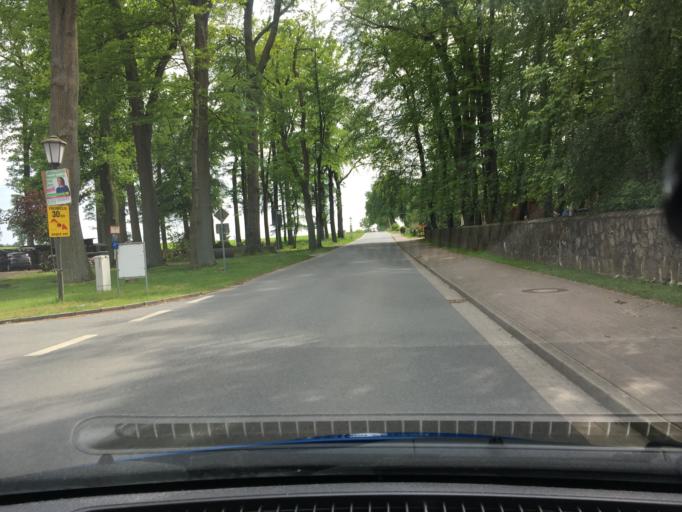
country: DE
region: Lower Saxony
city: Betzendorf
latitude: 53.1096
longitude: 10.3018
